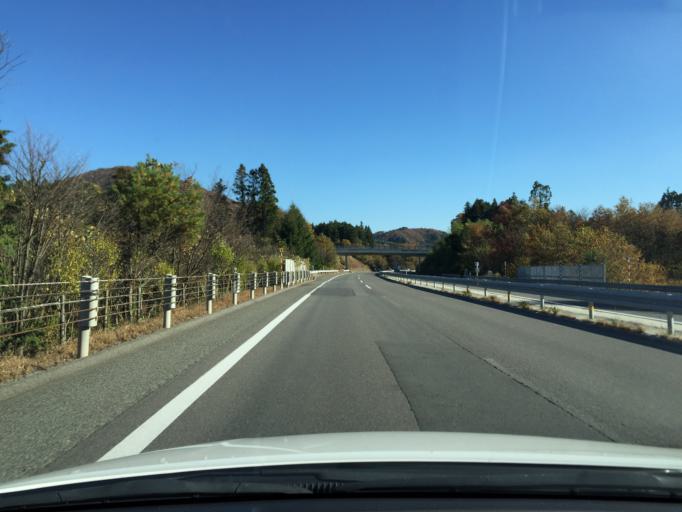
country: JP
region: Fukushima
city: Funehikimachi-funehiki
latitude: 37.4294
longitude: 140.5467
